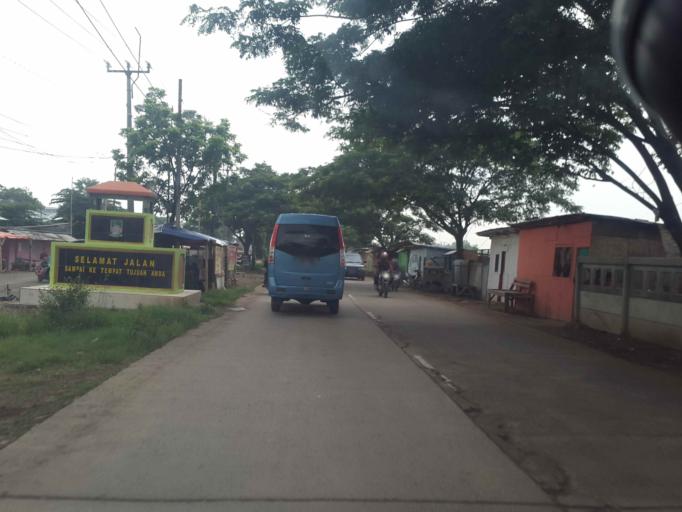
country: ID
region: West Java
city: Cikarang
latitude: -6.3162
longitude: 107.1563
